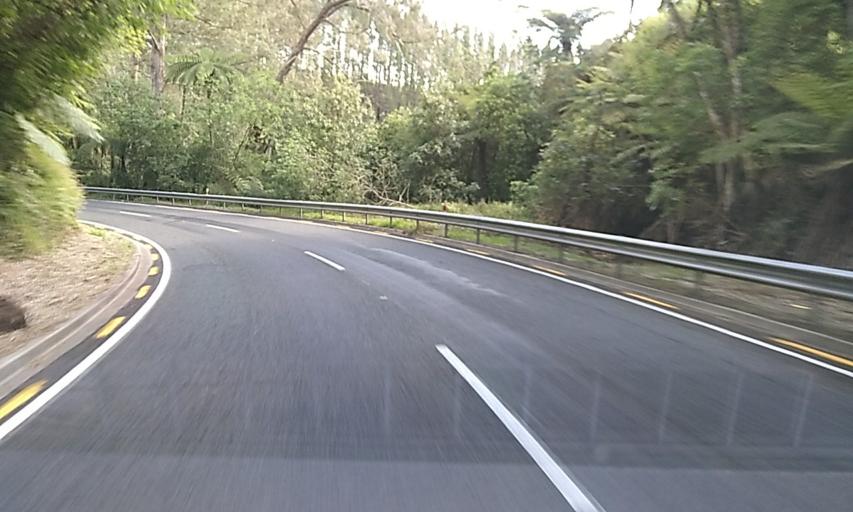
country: NZ
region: Bay of Plenty
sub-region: Tauranga City
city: Tauranga
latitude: -37.8045
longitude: 176.0424
